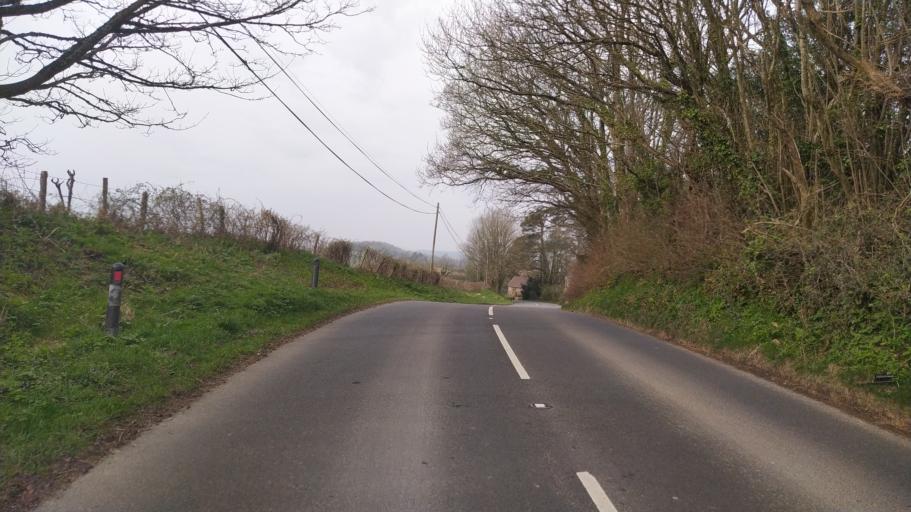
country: GB
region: England
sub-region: Dorset
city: Beaminster
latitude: 50.8020
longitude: -2.7125
